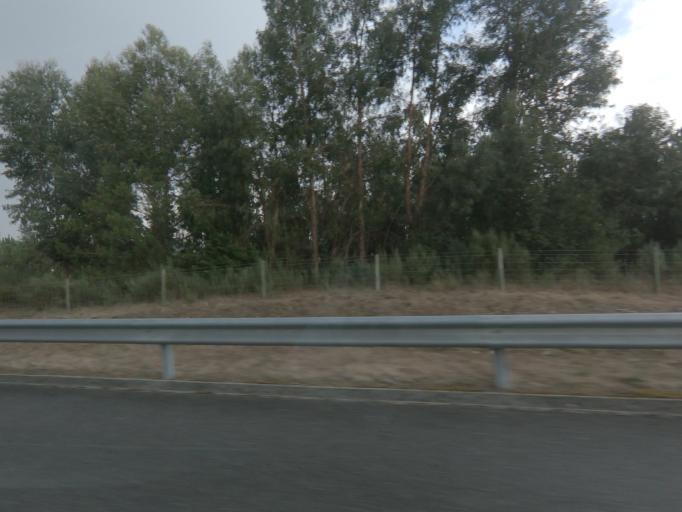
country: PT
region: Viseu
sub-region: Viseu
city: Abraveses
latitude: 40.7012
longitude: -7.9532
